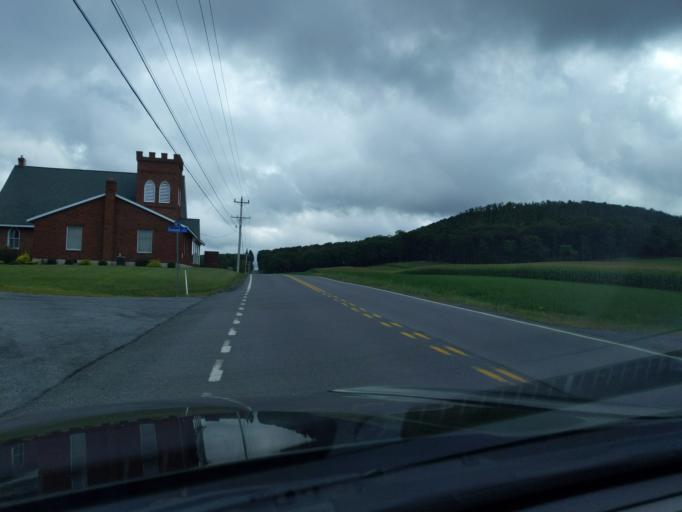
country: US
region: Pennsylvania
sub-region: Cambria County
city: Portage
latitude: 40.3167
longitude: -78.5726
